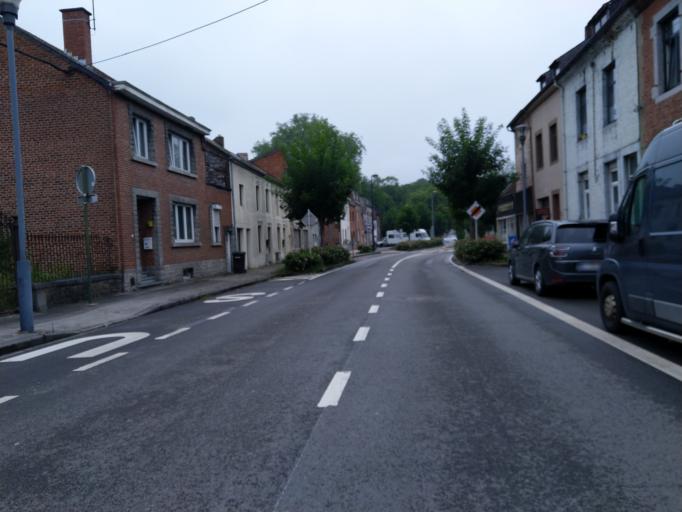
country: BE
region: Wallonia
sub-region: Province de Namur
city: Anhee
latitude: 50.3134
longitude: 4.8759
